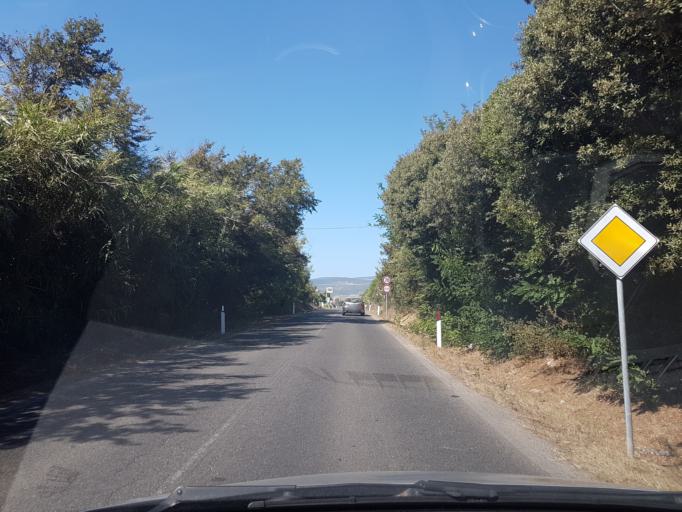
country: IT
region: Sardinia
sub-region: Provincia di Oristano
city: Nurachi
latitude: 39.9827
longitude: 8.5396
